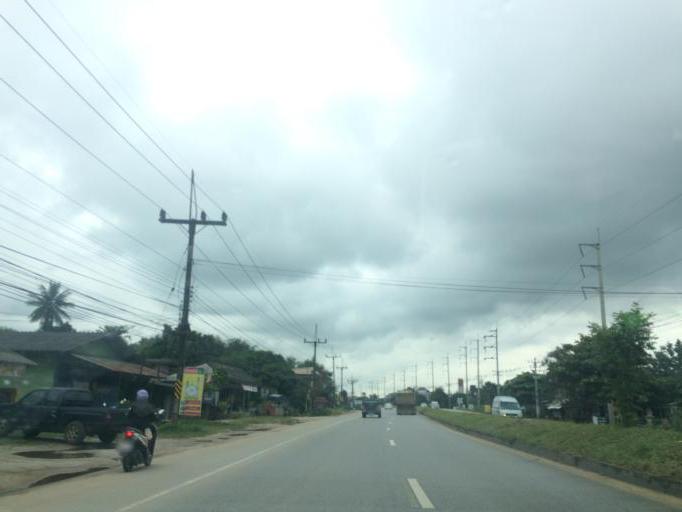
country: TH
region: Chiang Rai
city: Mae Chan
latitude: 20.0724
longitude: 99.8756
